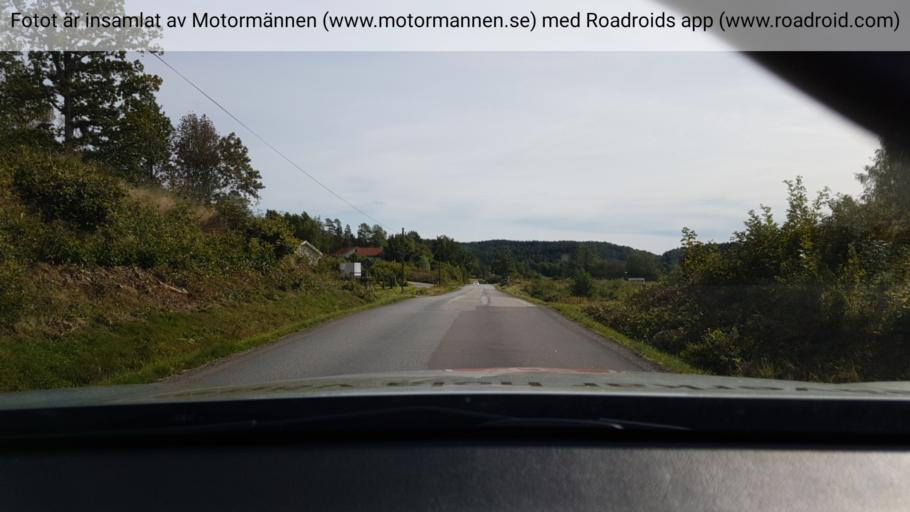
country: SE
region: Vaestra Goetaland
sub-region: Uddevalla Kommun
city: Ljungskile
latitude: 58.2415
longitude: 11.8673
